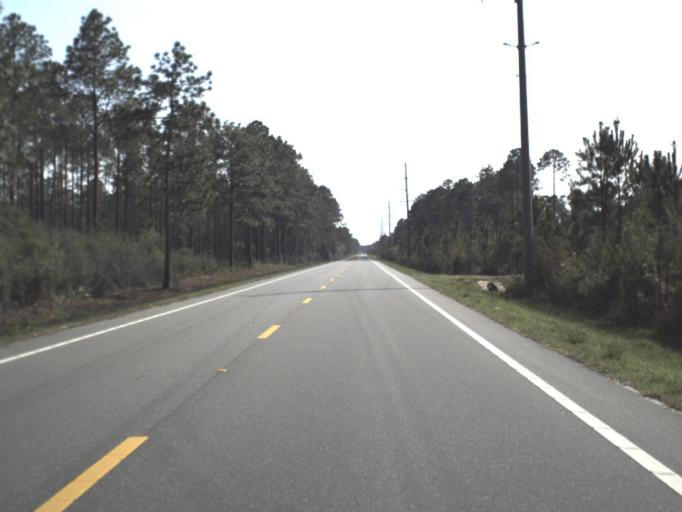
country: US
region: Florida
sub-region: Wakulla County
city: Crawfordville
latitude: 30.0315
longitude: -84.4977
